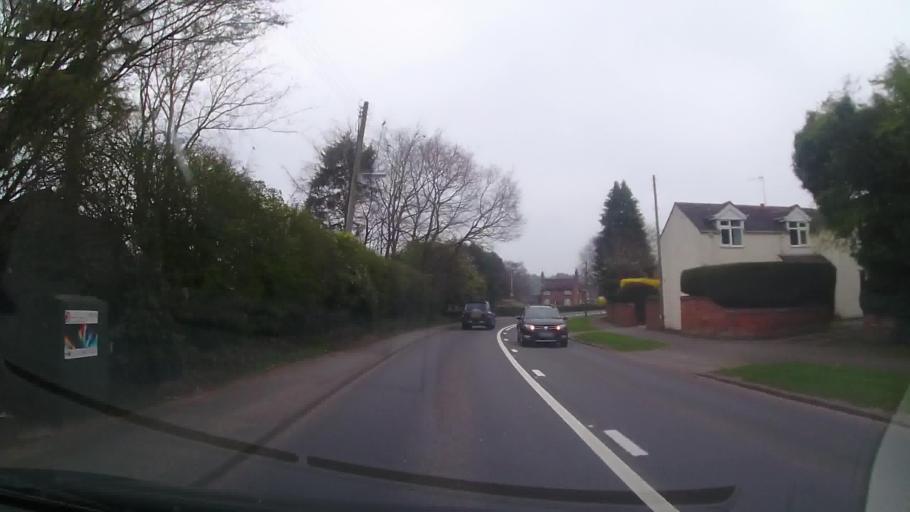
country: GB
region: England
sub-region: Staffordshire
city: Standon
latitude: 52.9580
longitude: -2.3096
